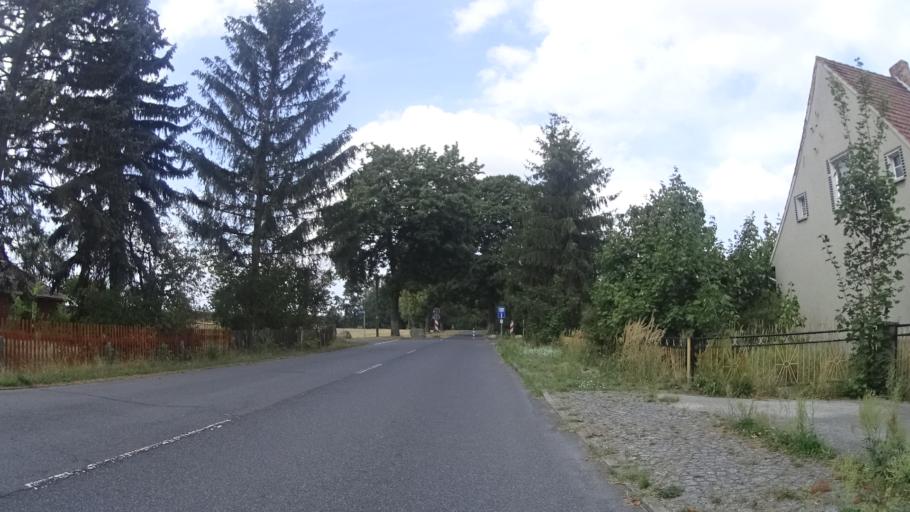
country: DE
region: Saxony
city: Gablenz
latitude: 51.5674
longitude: 14.6603
